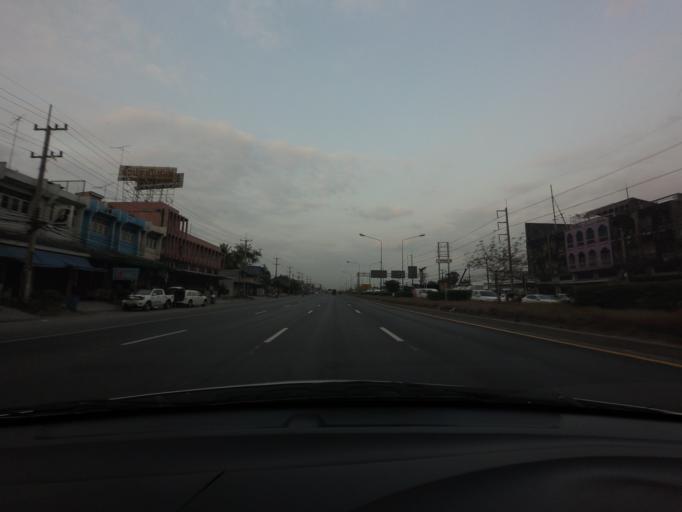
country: TH
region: Chon Buri
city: Chon Buri
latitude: 13.3567
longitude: 101.0093
